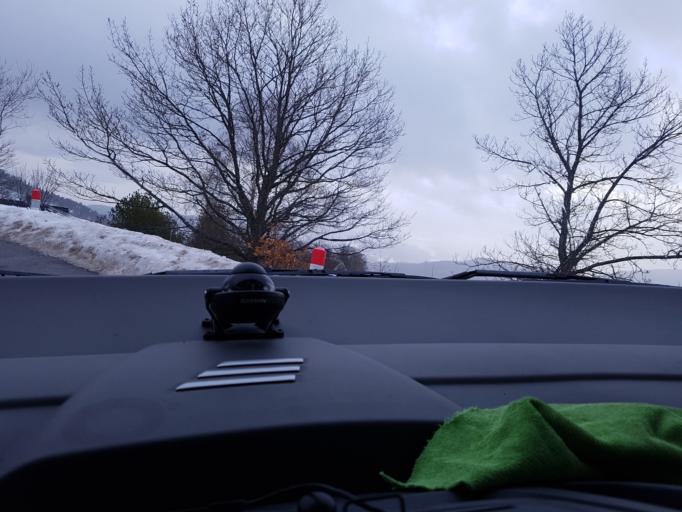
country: FR
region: Alsace
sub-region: Departement du Haut-Rhin
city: Soultzeren
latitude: 48.0775
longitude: 7.1062
